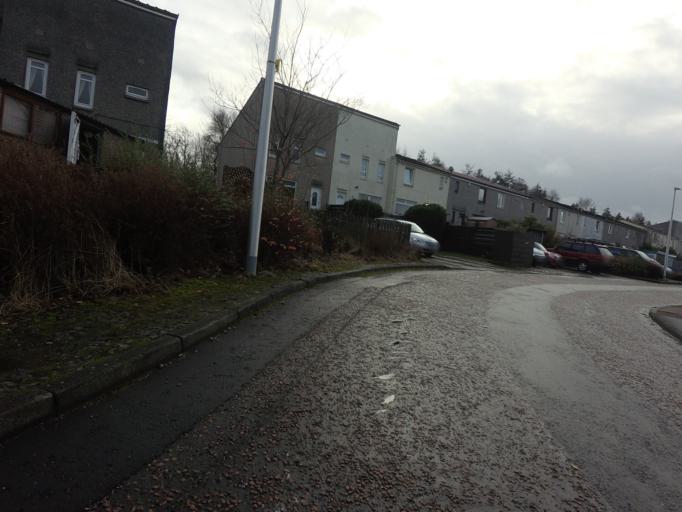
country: GB
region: Scotland
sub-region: West Lothian
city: Livingston
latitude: 55.8750
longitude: -3.5172
